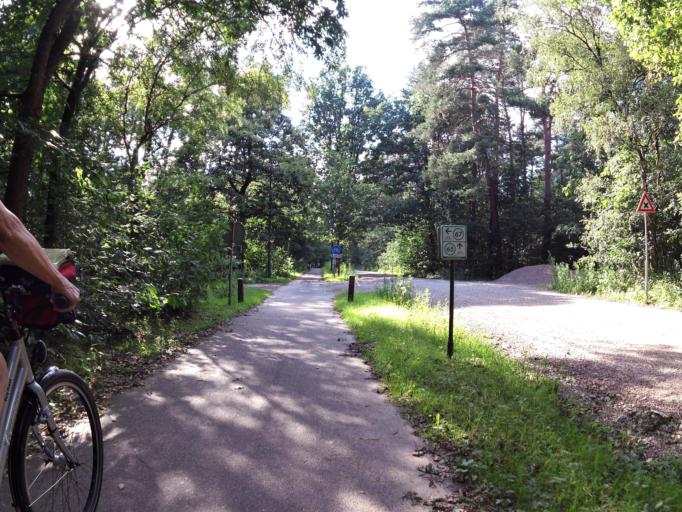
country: NL
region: North Brabant
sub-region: Gemeente Eindhoven
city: Lakerlopen
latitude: 51.3932
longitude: 5.4959
